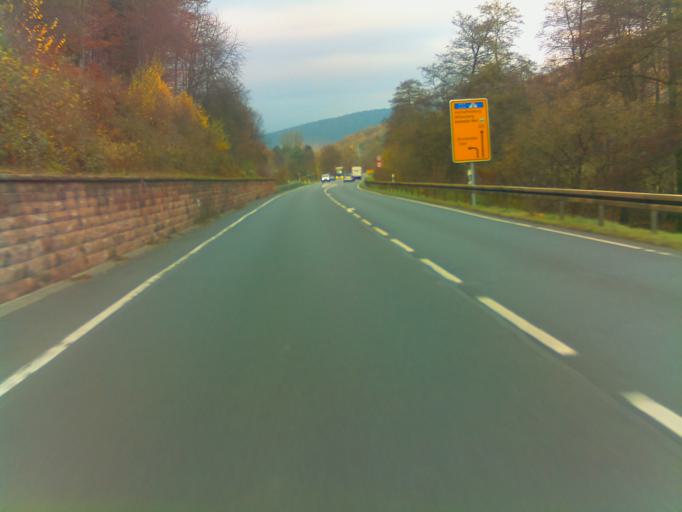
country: DE
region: Bavaria
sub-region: Regierungsbezirk Unterfranken
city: Weilbach
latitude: 49.6838
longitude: 9.2187
